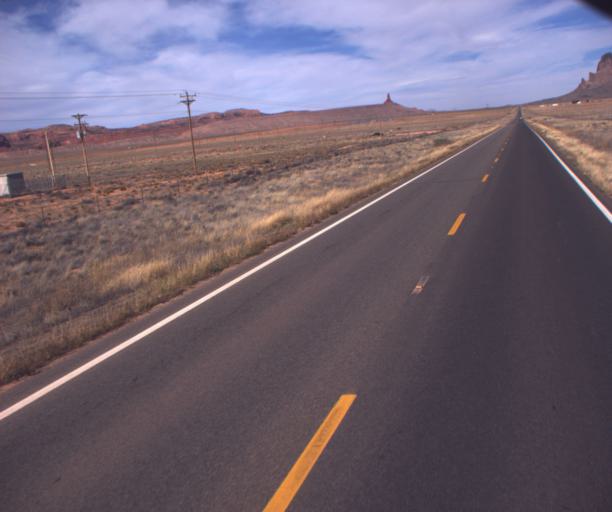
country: US
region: Arizona
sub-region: Navajo County
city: Kayenta
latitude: 36.7629
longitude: -110.2273
